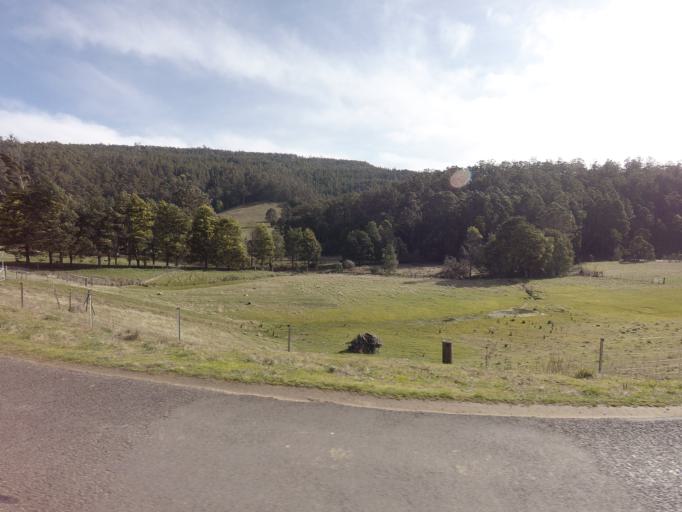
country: AU
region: Tasmania
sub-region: Huon Valley
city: Huonville
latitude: -43.0461
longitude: 147.1155
